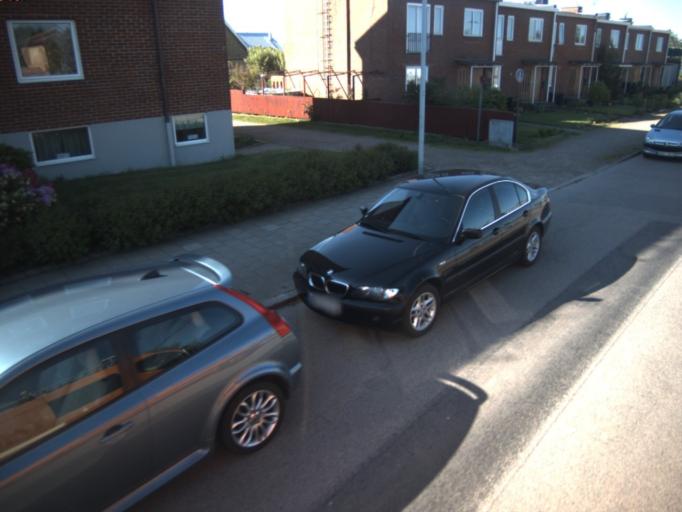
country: SE
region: Skane
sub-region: Helsingborg
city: Rydeback
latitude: 56.0032
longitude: 12.7324
